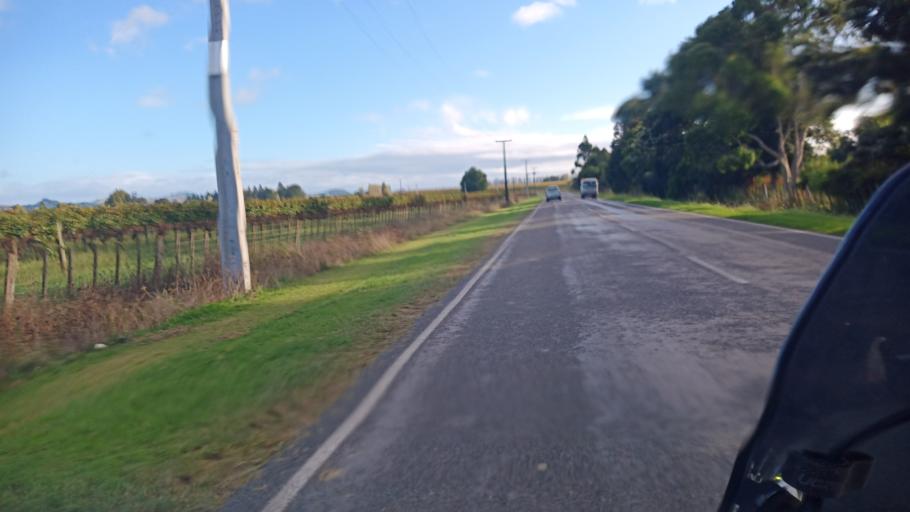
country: NZ
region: Gisborne
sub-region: Gisborne District
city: Gisborne
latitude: -38.6484
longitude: 177.9173
